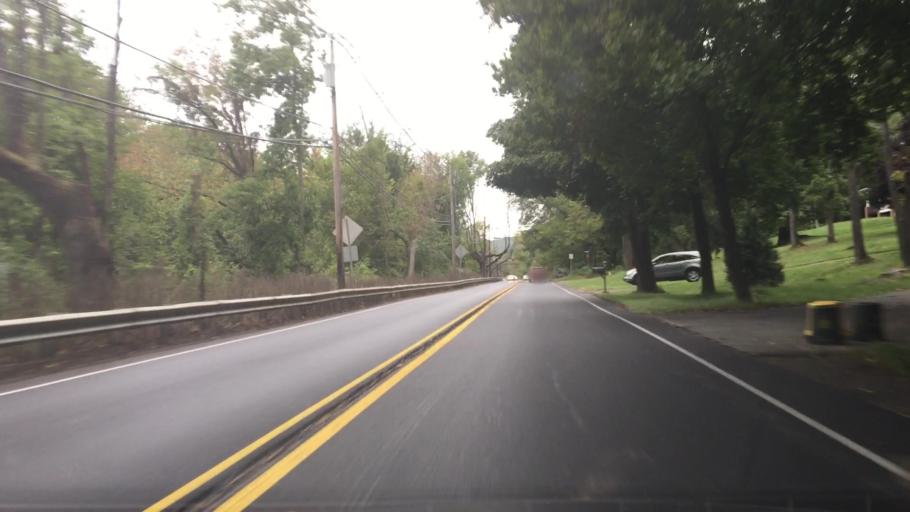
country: US
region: Pennsylvania
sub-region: Bucks County
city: Yardley
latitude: 40.3050
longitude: -74.8744
